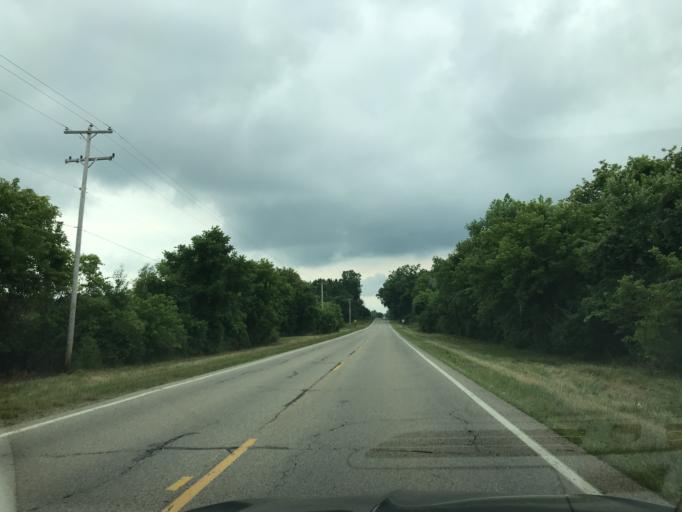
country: US
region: Michigan
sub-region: Eaton County
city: Grand Ledge
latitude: 42.8041
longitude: -84.7709
